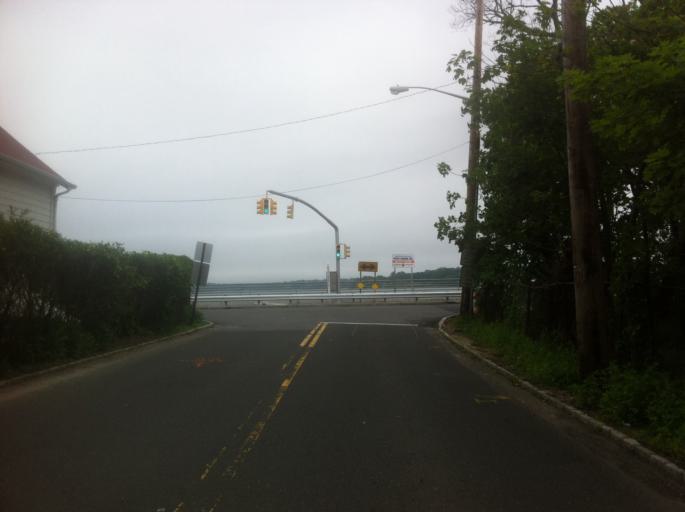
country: US
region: New York
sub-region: Nassau County
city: Oyster Bay
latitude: 40.8823
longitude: -73.5512
